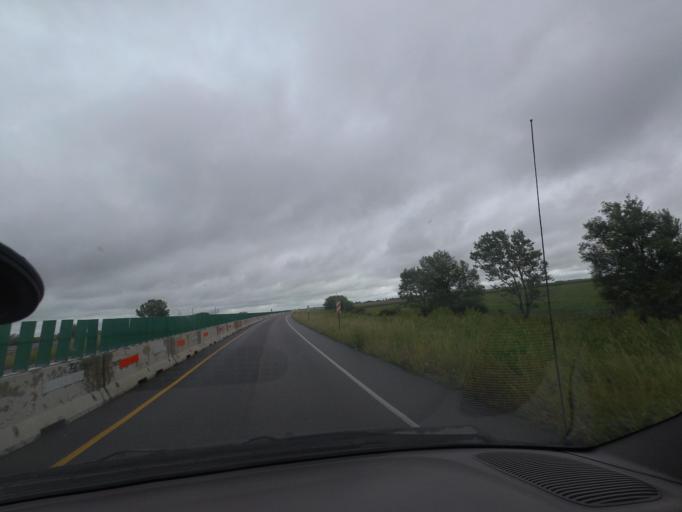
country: US
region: Illinois
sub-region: Piatt County
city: Cerro Gordo
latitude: 40.0140
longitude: -88.7672
